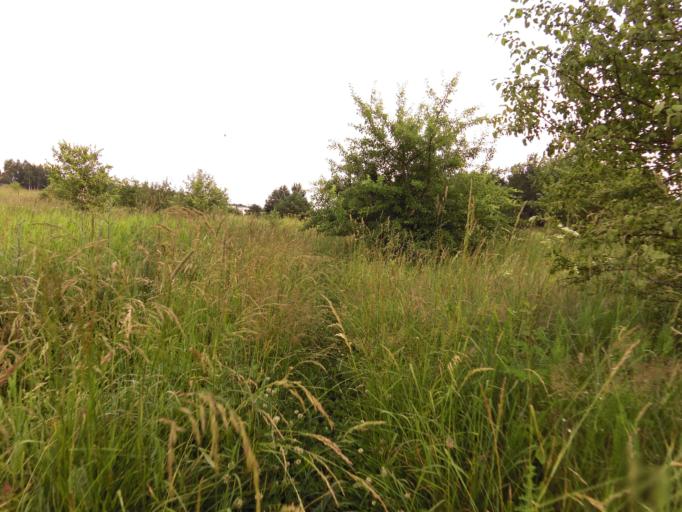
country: LT
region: Vilnius County
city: Pasilaiciai
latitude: 54.7533
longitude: 25.2228
